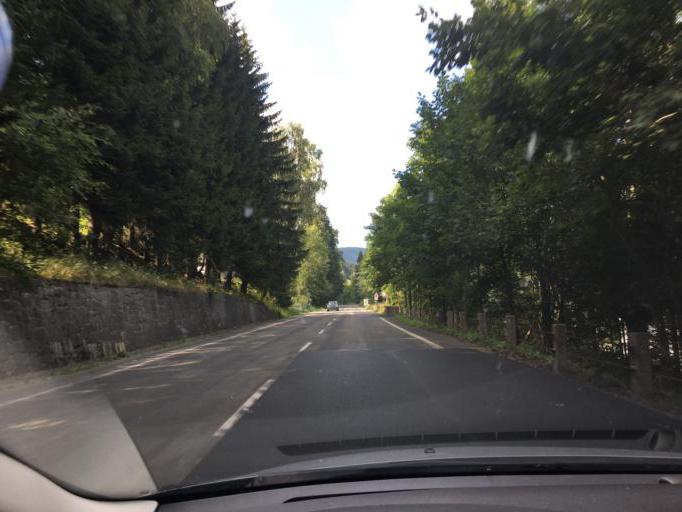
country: CZ
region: Kralovehradecky
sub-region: Okres Trutnov
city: Spindleruv Mlyn
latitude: 50.7027
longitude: 15.5833
